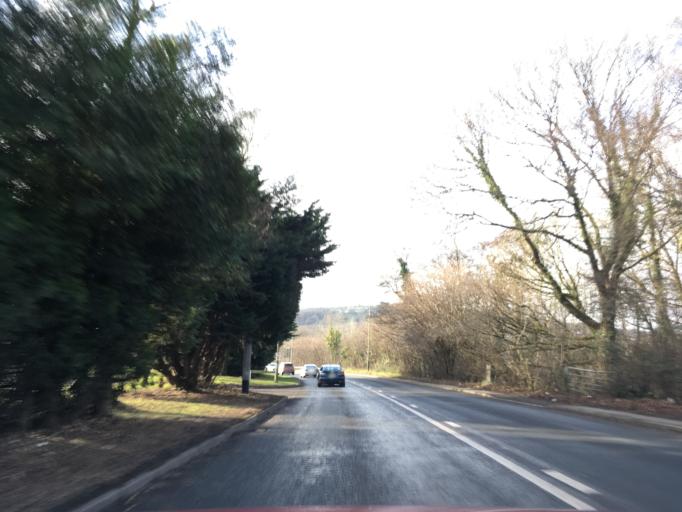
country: GB
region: Wales
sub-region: Caerphilly County Borough
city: Maesycwmmer
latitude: 51.6410
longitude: -3.2277
